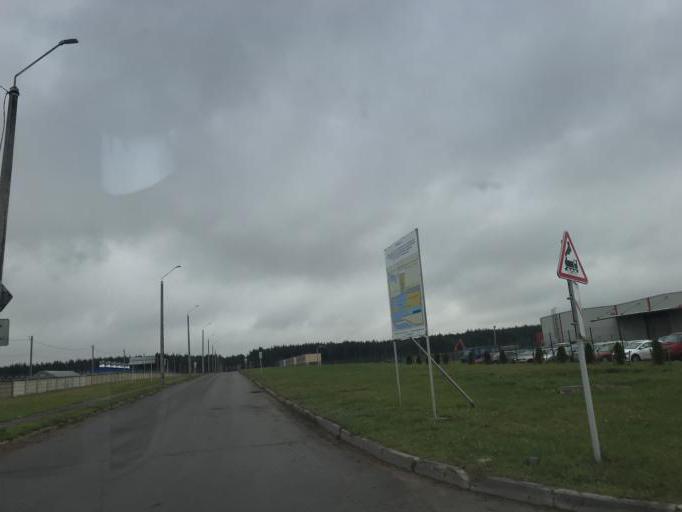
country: BY
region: Mogilev
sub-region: Mahilyowski Rayon
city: Veyno
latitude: 53.8234
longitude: 30.3526
